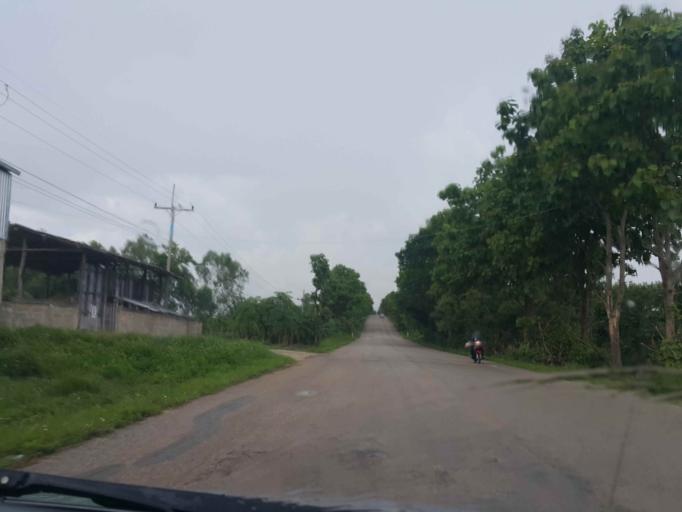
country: TH
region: Phayao
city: Dok Kham Tai
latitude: 19.0130
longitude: 100.0622
